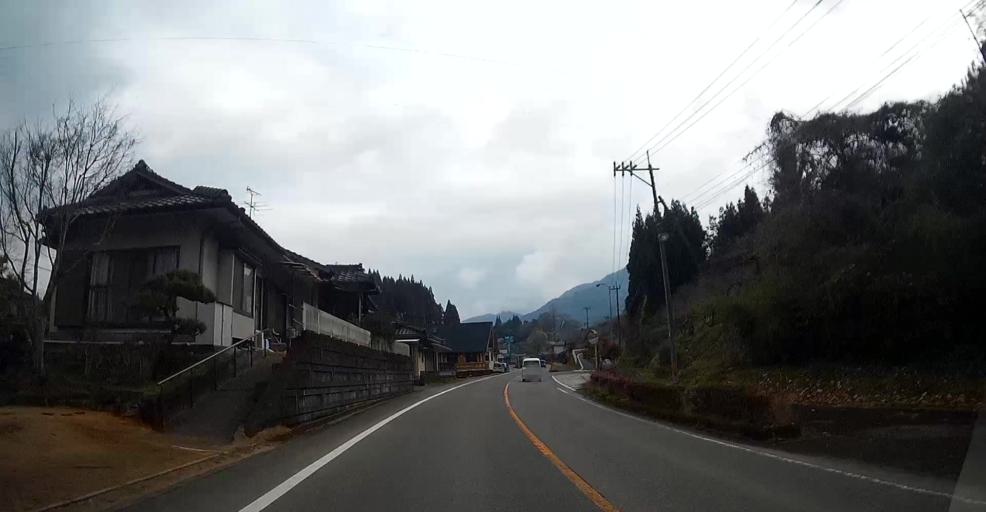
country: JP
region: Kumamoto
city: Matsubase
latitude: 32.6212
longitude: 130.8661
